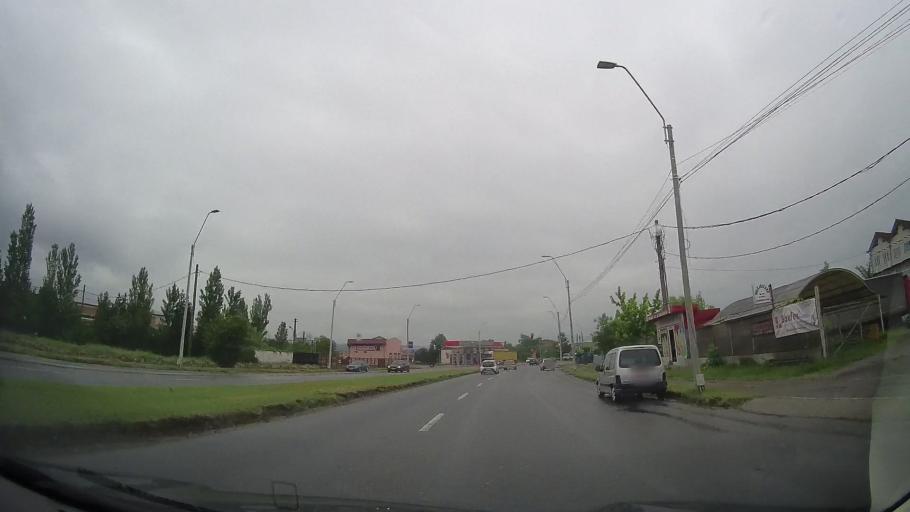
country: RO
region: Mehedinti
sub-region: Comuna Simian
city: Dudasu
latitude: 44.6319
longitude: 22.6837
